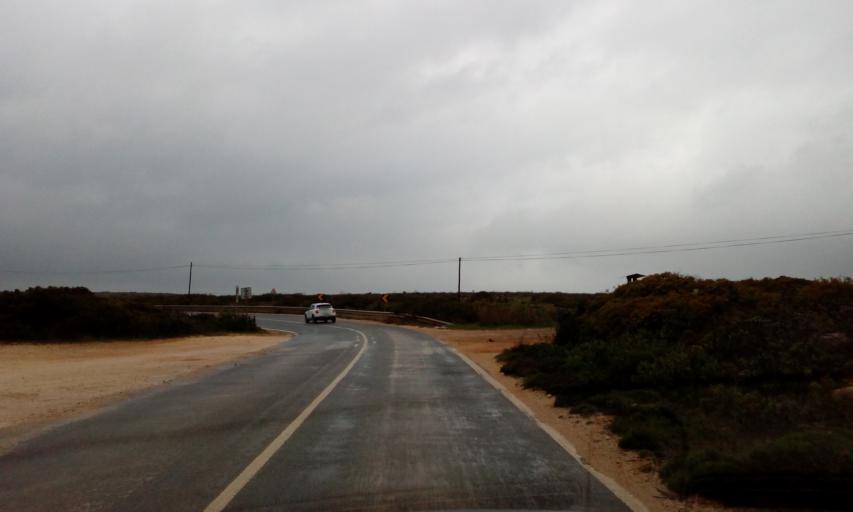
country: PT
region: Faro
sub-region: Vila do Bispo
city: Sagres
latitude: 37.0269
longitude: -8.9627
